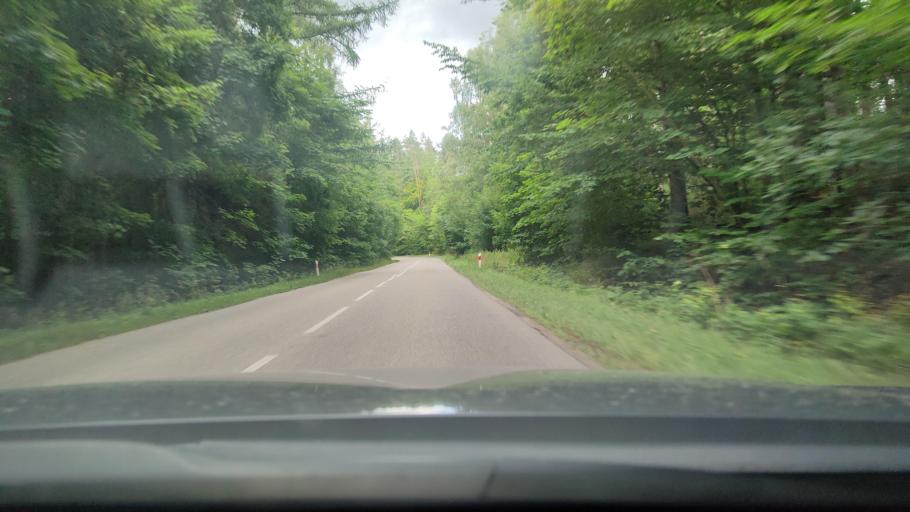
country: PL
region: Pomeranian Voivodeship
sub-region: Powiat pucki
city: Krokowa
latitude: 54.7248
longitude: 18.1705
